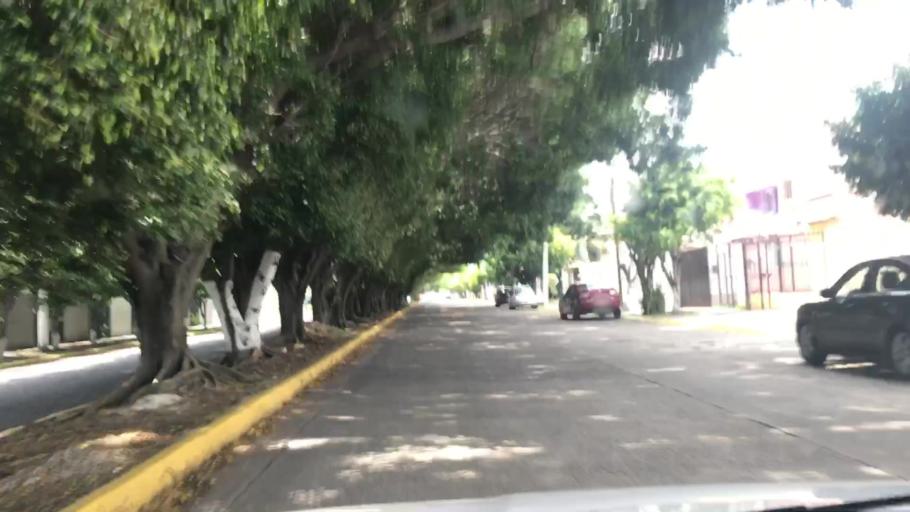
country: MX
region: Jalisco
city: Guadalajara
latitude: 20.6502
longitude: -103.4240
